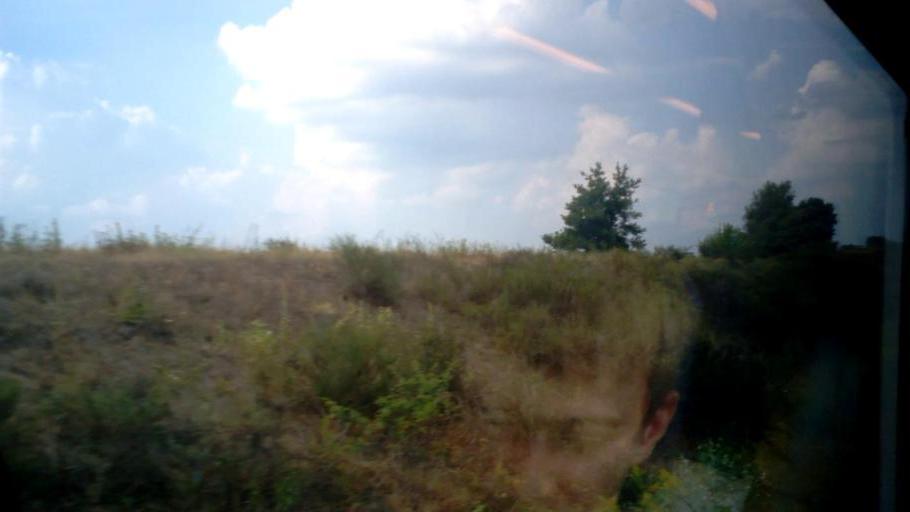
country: DE
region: Brandenburg
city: Grossbeeren
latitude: 52.3464
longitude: 13.2828
